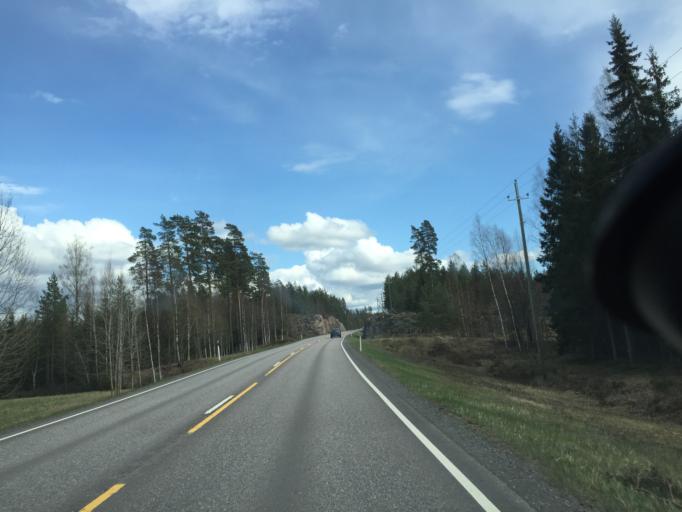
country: FI
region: Uusimaa
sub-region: Raaseporin
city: Ekenaes
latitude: 60.0392
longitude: 23.3523
